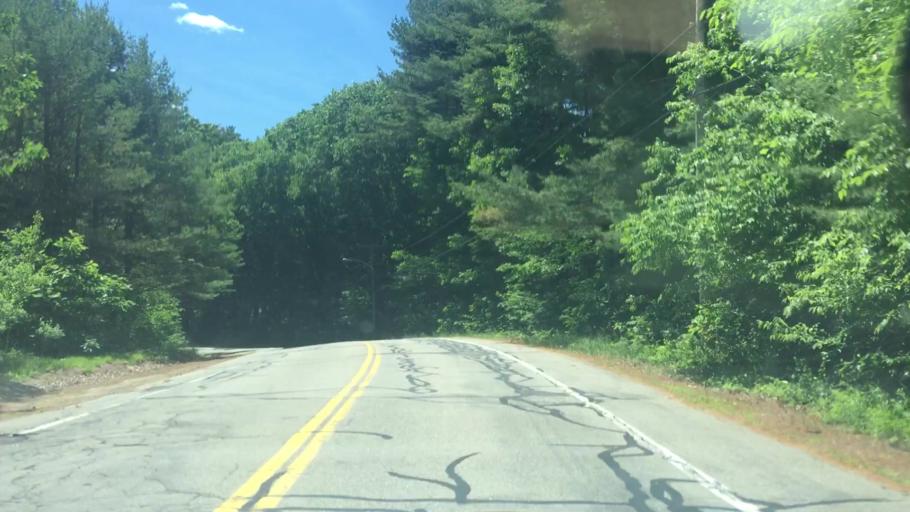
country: US
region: Maine
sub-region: York County
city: Kennebunk
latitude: 43.3737
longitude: -70.5275
